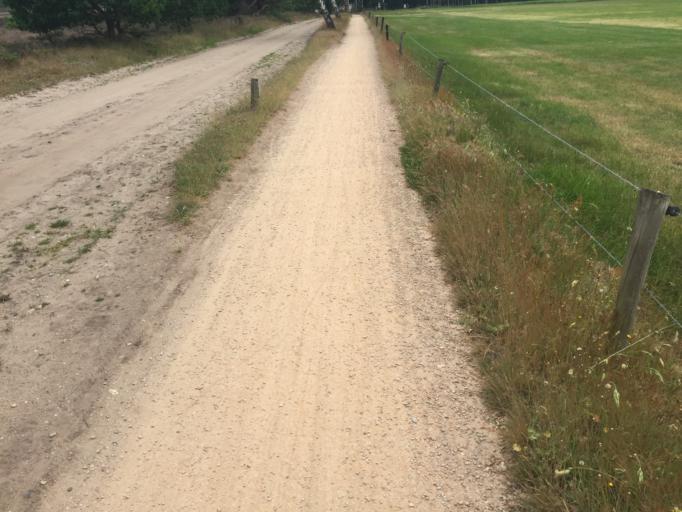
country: NL
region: Overijssel
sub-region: Gemeente Raalte
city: Raalte
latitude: 52.3503
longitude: 6.3829
